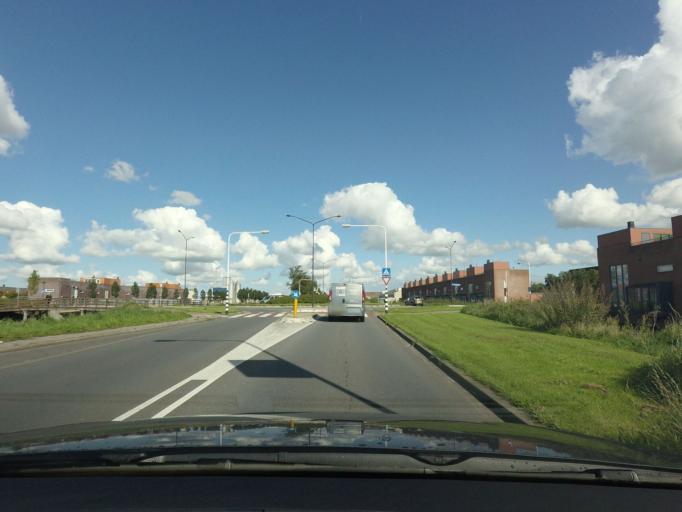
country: NL
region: North Holland
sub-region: Gemeente Langedijk
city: Broek op Langedijk
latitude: 52.6457
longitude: 4.8191
